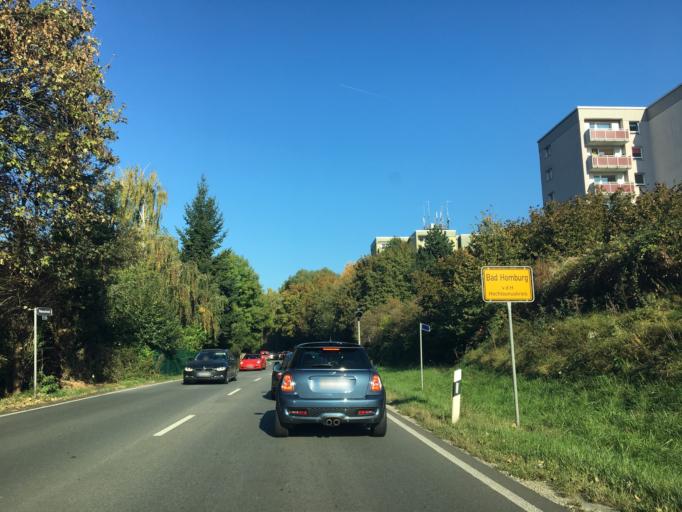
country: DE
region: Hesse
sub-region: Regierungsbezirk Darmstadt
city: Oberursel
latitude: 50.2354
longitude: 8.5872
